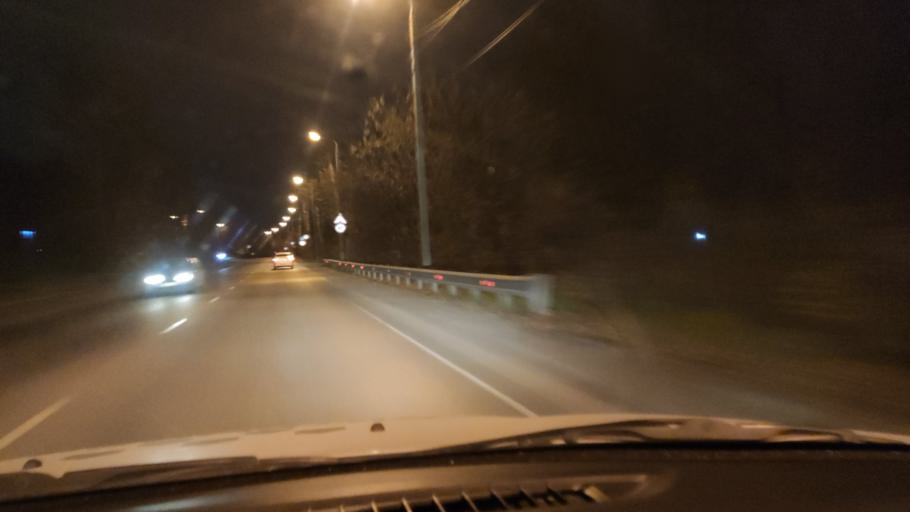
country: RU
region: Perm
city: Kondratovo
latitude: 57.9690
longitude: 56.1277
